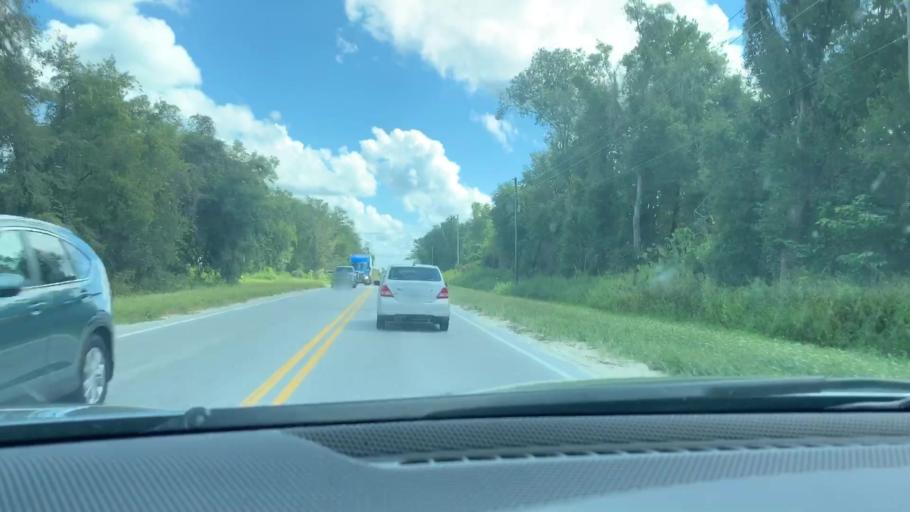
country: US
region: Florida
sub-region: Marion County
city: Ocala
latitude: 29.2669
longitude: -82.1665
